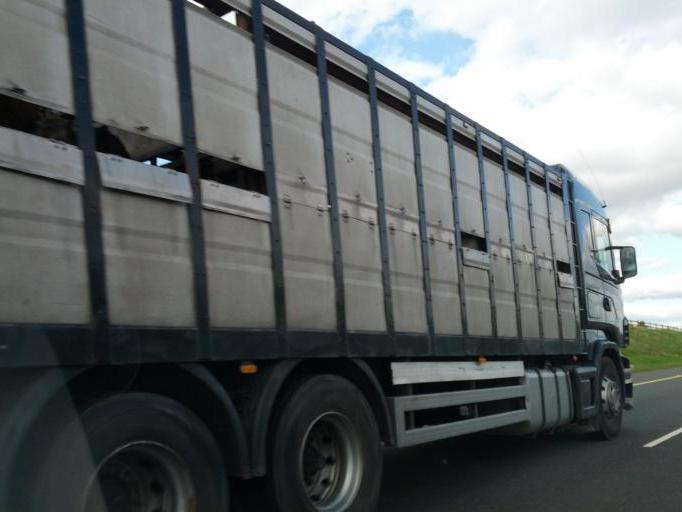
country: IE
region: Connaught
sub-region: County Galway
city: Ballinasloe
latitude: 53.3266
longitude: -8.1353
